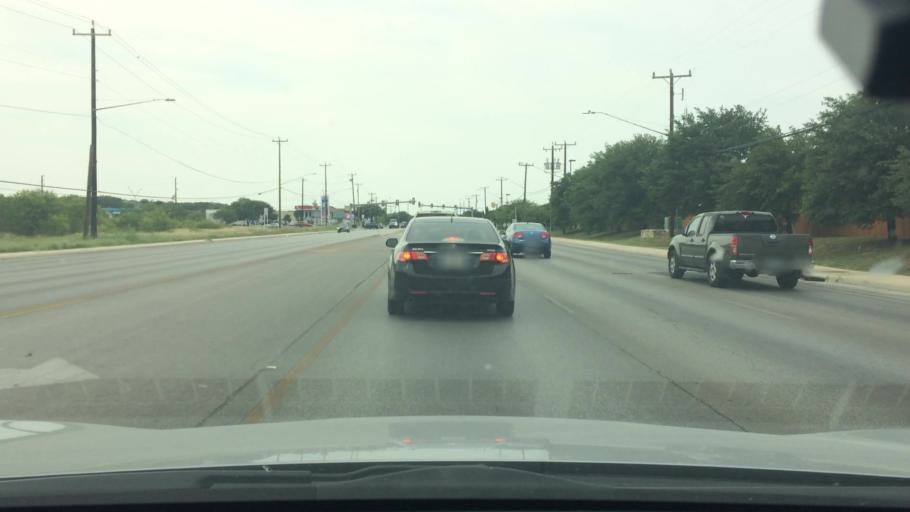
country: US
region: Texas
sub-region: Bexar County
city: Leon Valley
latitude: 29.4769
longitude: -98.6616
